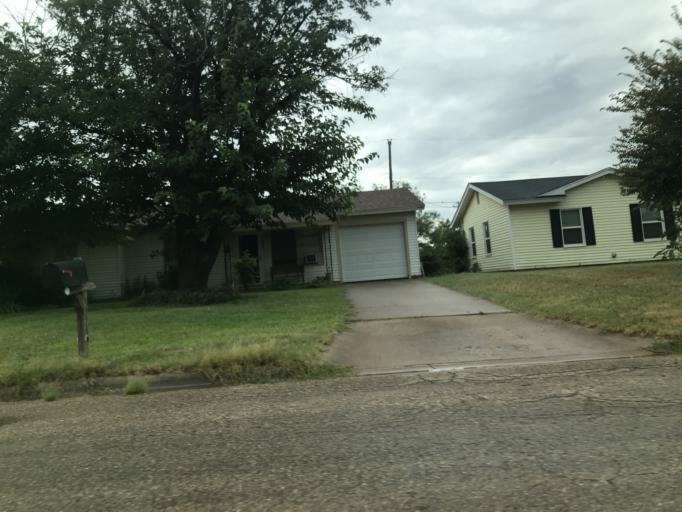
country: US
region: Texas
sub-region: Taylor County
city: Abilene
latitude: 32.4170
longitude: -99.7853
